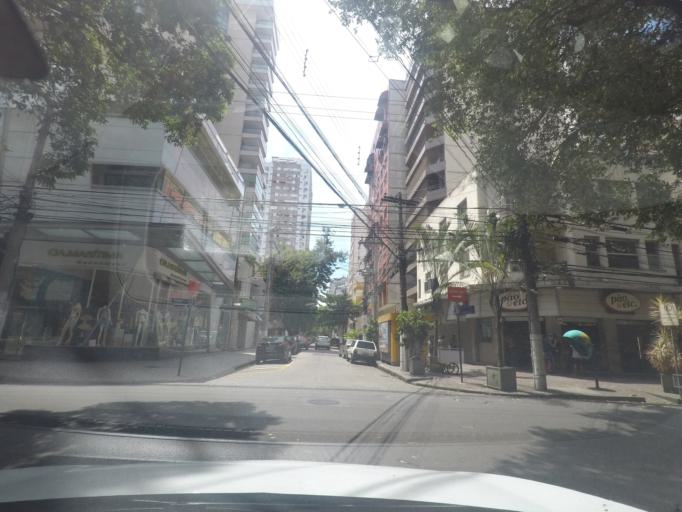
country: BR
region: Rio de Janeiro
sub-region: Niteroi
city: Niteroi
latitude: -22.9055
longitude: -43.1101
